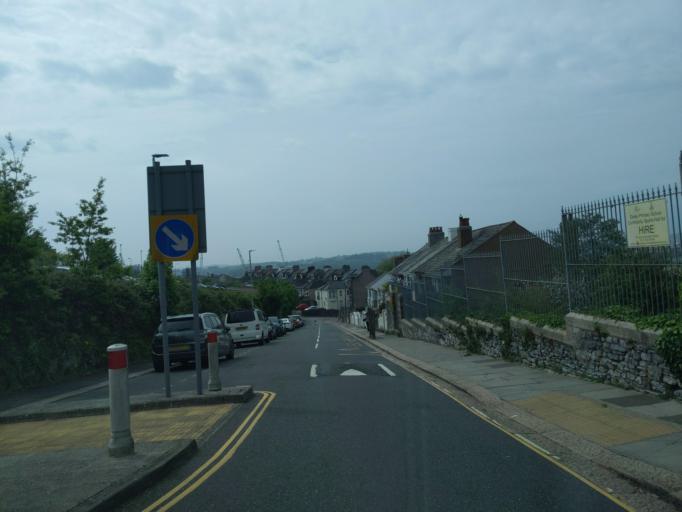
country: GB
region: England
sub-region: Cornwall
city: Torpoint
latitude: 50.3879
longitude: -4.1791
